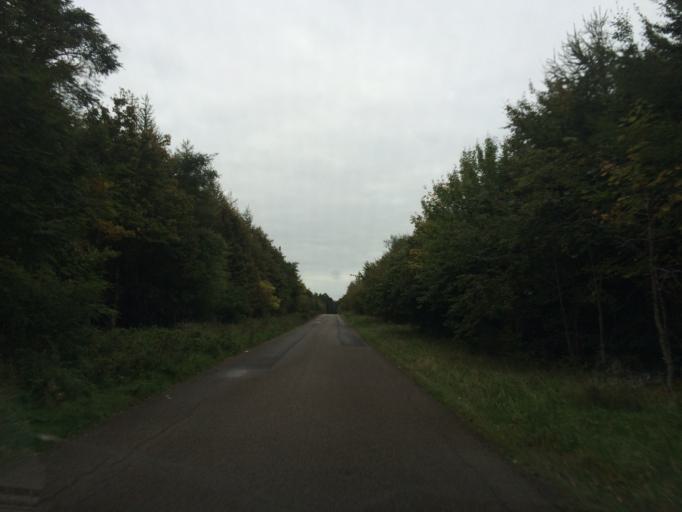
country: DK
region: Central Jutland
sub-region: Holstebro Kommune
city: Ulfborg
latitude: 56.2207
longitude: 8.4445
